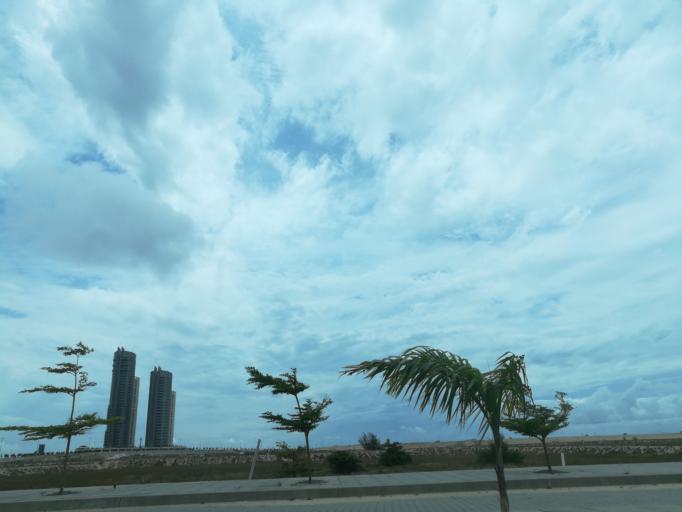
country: NG
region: Lagos
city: Lagos
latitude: 6.4093
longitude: 3.4036
